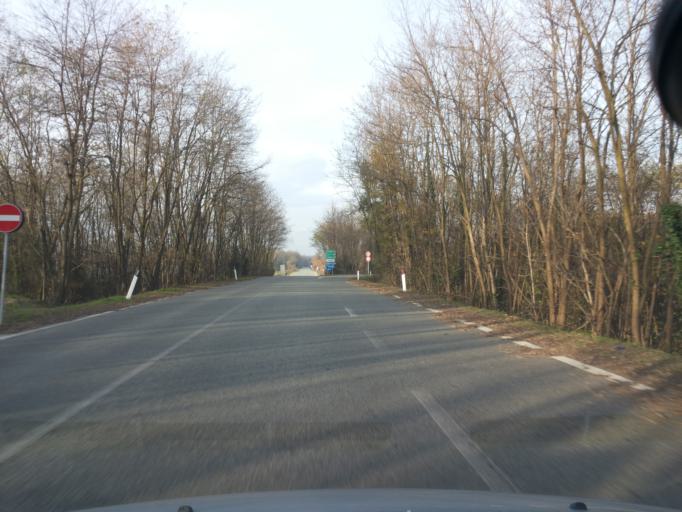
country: IT
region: Piedmont
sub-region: Provincia di Biella
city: Verrone
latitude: 45.4892
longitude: 8.1136
